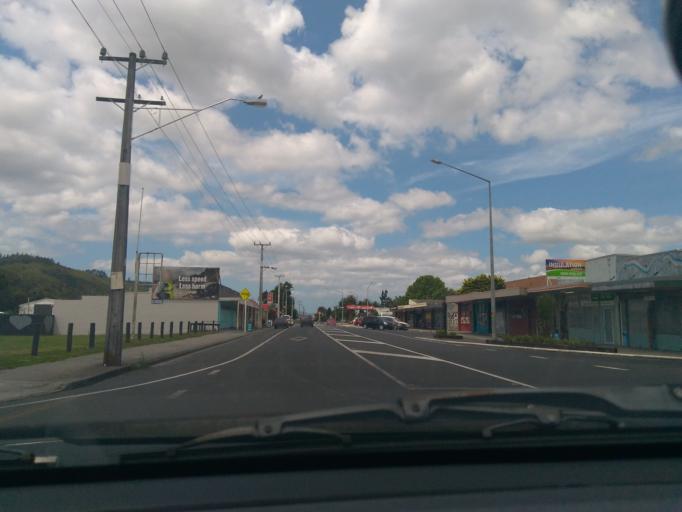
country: NZ
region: Northland
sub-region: Far North District
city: Moerewa
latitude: -35.3880
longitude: 174.0135
